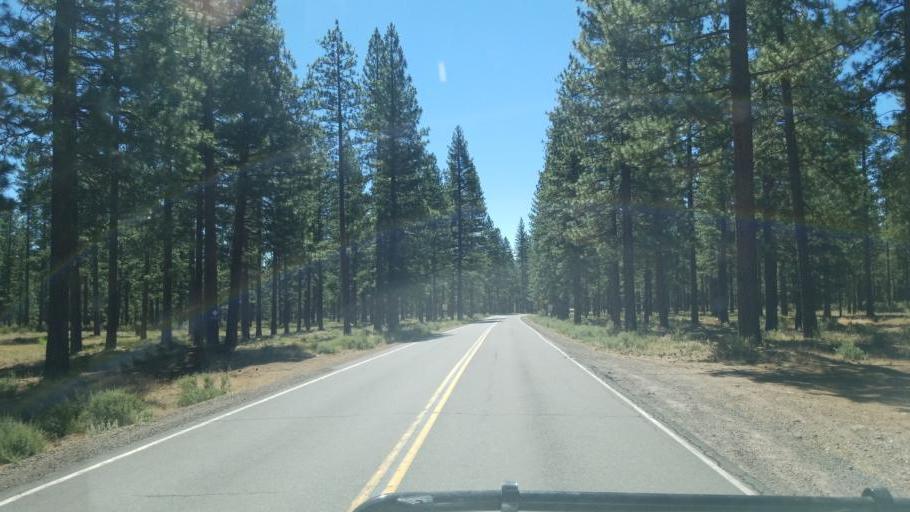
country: US
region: California
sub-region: Lassen County
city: Susanville
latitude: 40.4259
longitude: -120.7254
